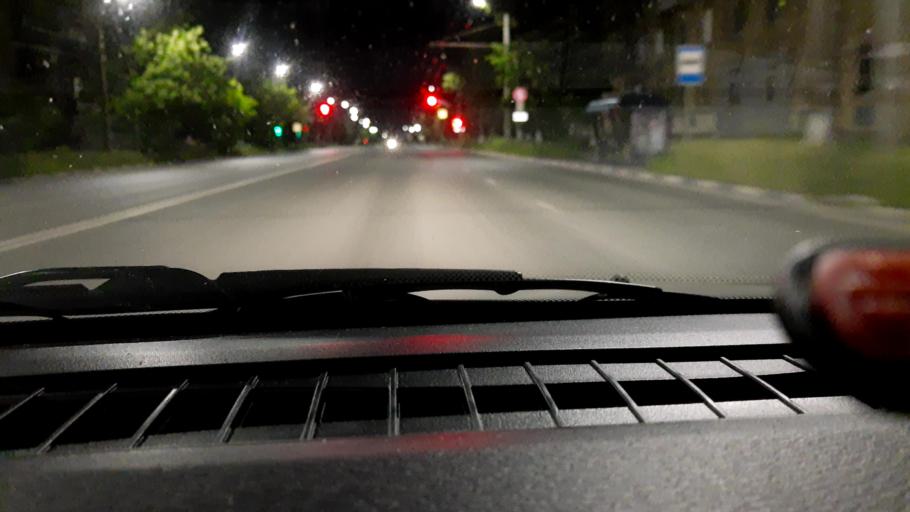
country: RU
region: Nizjnij Novgorod
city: Dzerzhinsk
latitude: 56.2420
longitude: 43.4812
